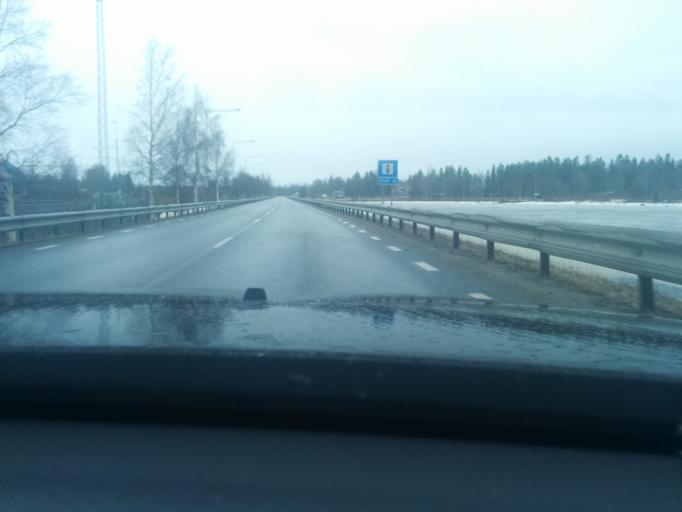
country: SE
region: Vaesterbotten
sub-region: Umea Kommun
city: Holmsund
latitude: 63.6963
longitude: 20.3566
